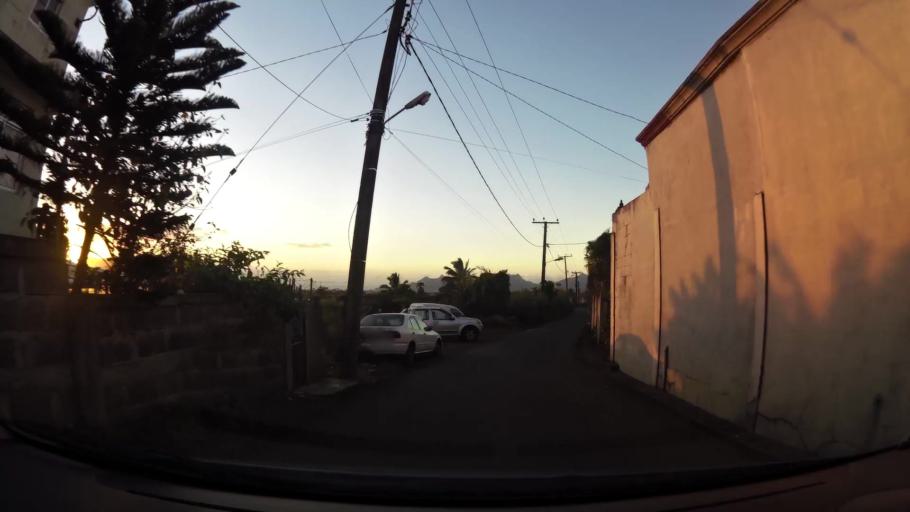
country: MU
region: Plaines Wilhems
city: Curepipe
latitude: -20.3008
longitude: 57.5232
